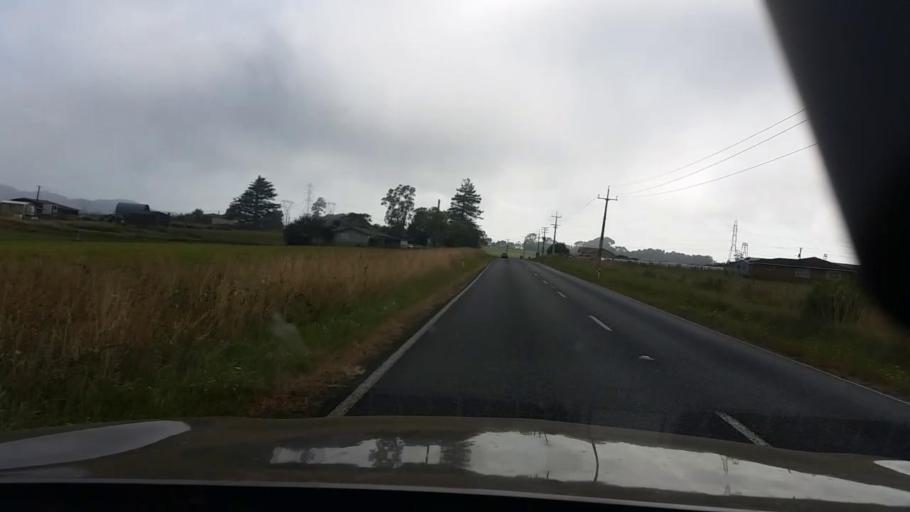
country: NZ
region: Waikato
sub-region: Hamilton City
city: Hamilton
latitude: -37.6203
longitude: 175.3347
